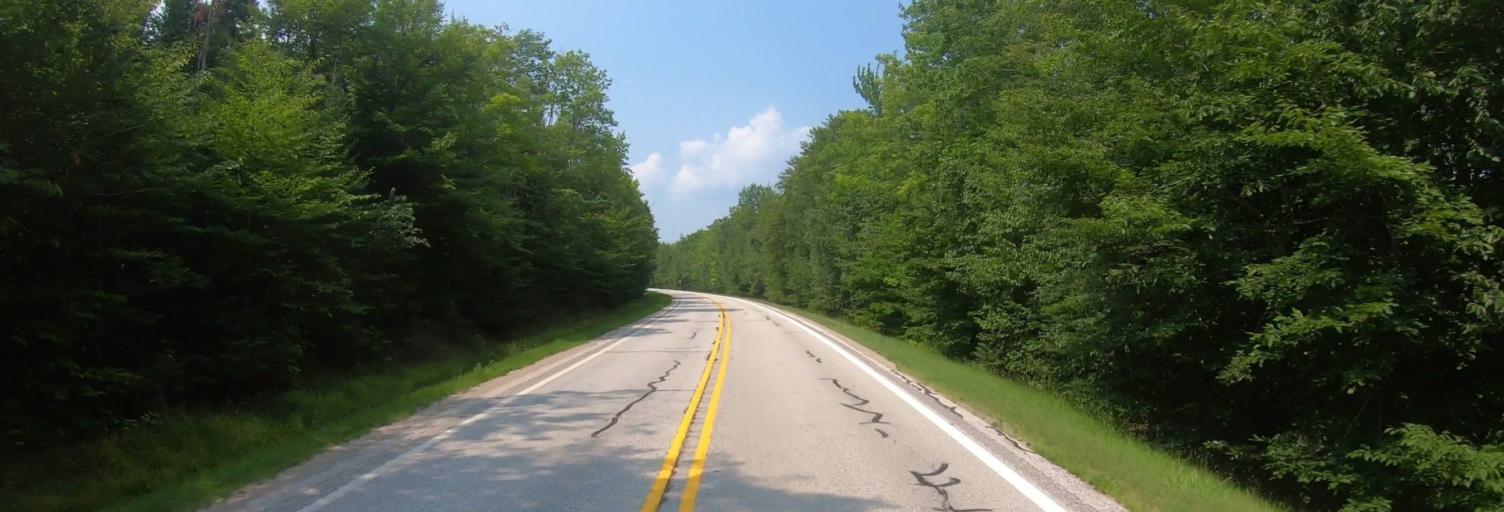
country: US
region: Michigan
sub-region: Luce County
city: Newberry
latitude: 46.5632
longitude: -85.3523
